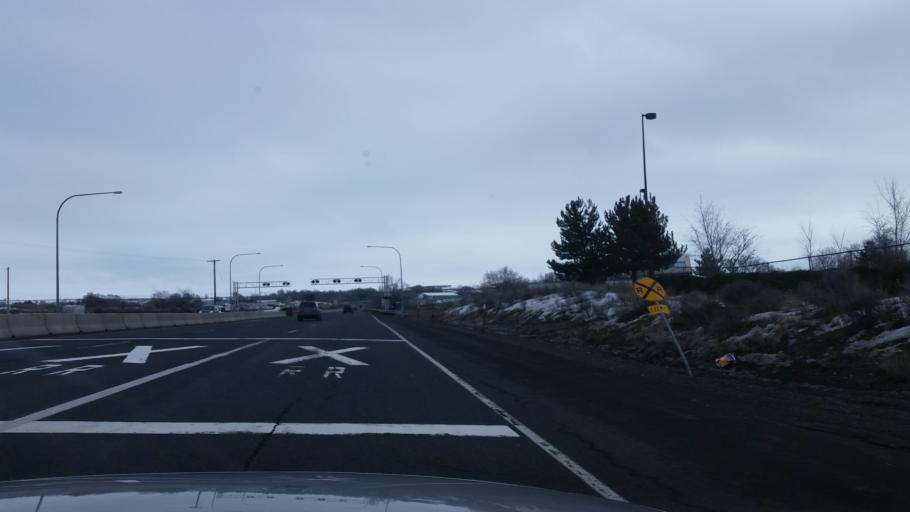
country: US
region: Washington
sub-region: Grant County
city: Moses Lake
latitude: 47.1428
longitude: -119.2736
